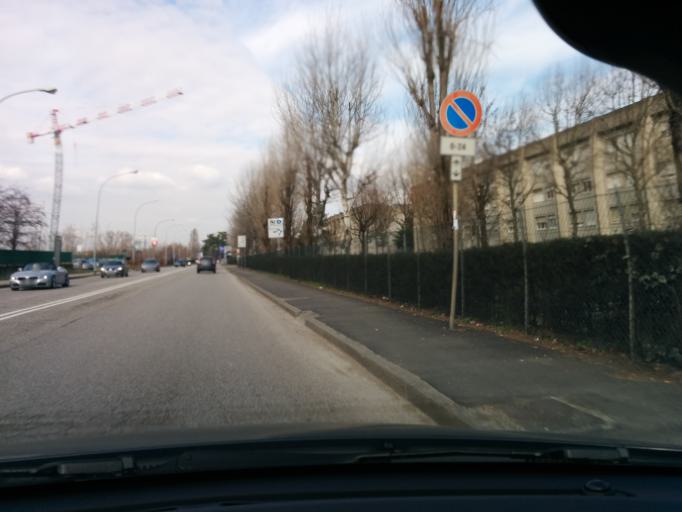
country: IT
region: Emilia-Romagna
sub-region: Provincia di Bologna
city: Bologna
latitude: 44.5230
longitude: 11.3300
